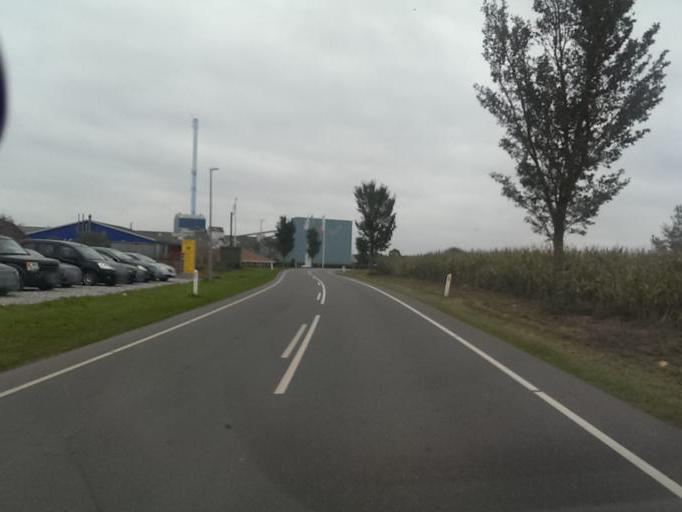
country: DK
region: South Denmark
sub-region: Esbjerg Kommune
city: Bramming
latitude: 55.4603
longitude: 8.7142
